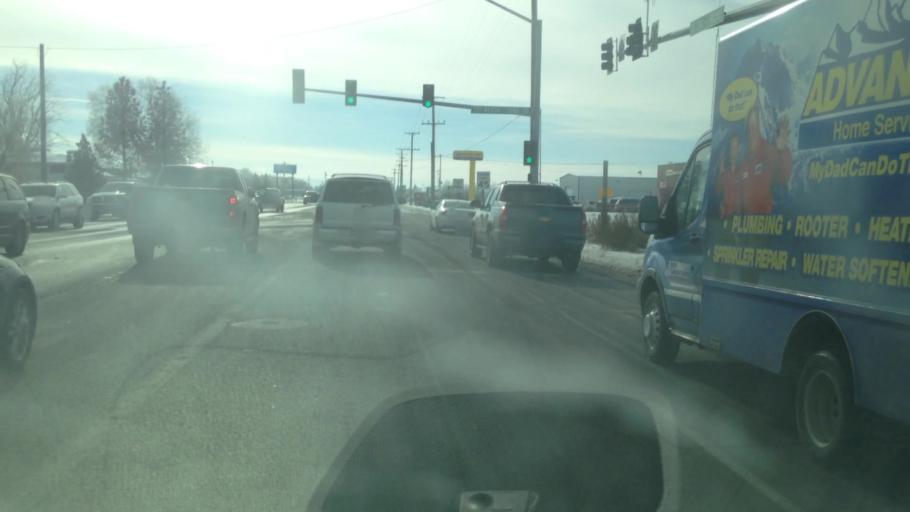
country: US
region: Idaho
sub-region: Bonneville County
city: Idaho Falls
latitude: 43.5255
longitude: -112.0236
